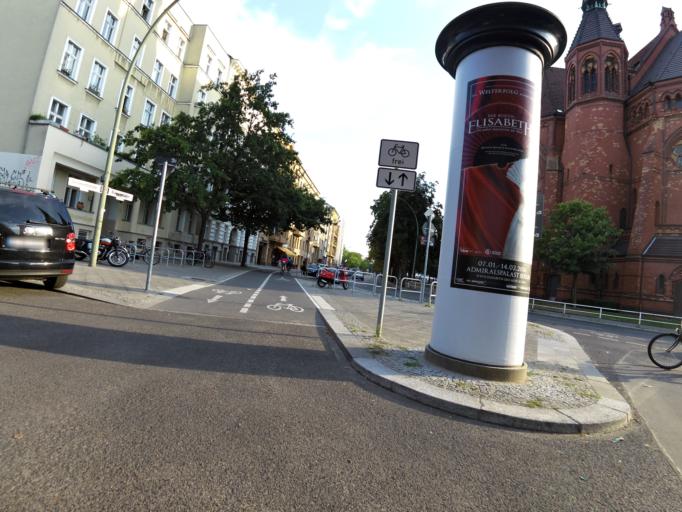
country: DE
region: Berlin
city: Tiergarten Bezirk
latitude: 52.4971
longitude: 13.3669
